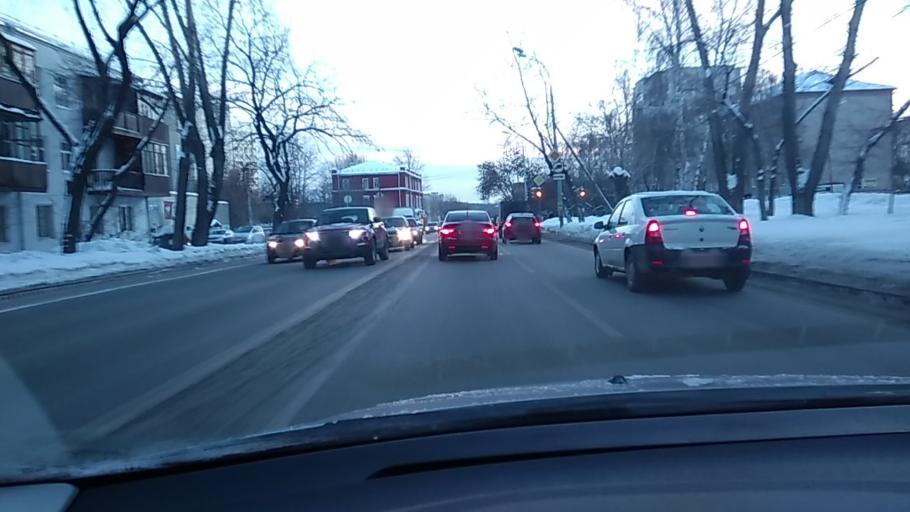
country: RU
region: Sverdlovsk
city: Yekaterinburg
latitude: 56.8242
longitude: 60.6386
